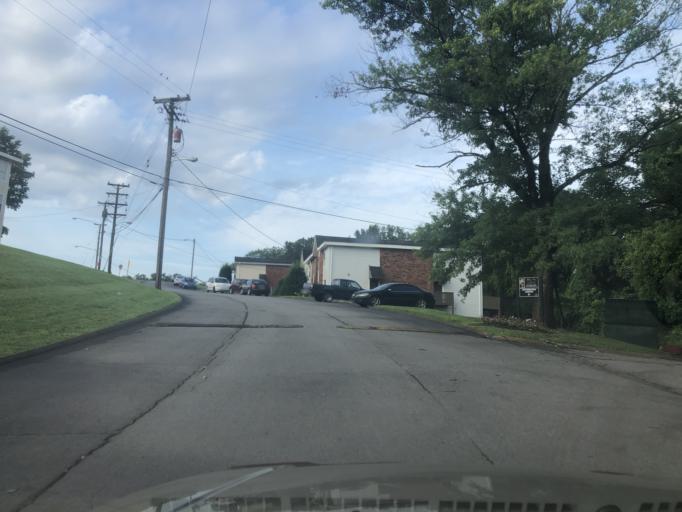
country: US
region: Tennessee
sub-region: Davidson County
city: Goodlettsville
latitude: 36.2505
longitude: -86.7158
